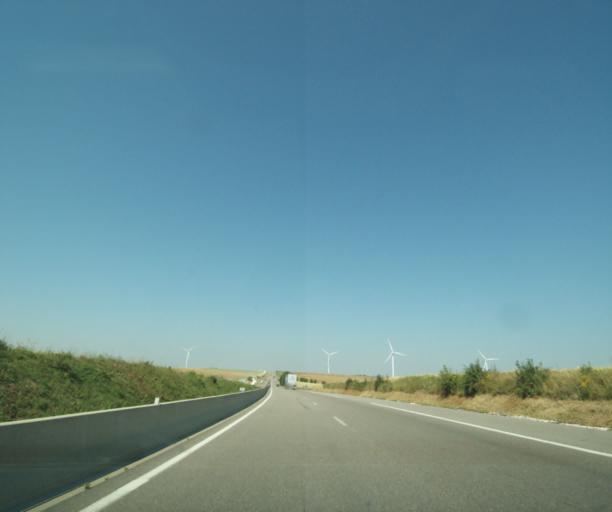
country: FR
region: Lorraine
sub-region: Departement de la Meuse
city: Ligny-en-Barrois
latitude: 48.7046
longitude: 5.4325
